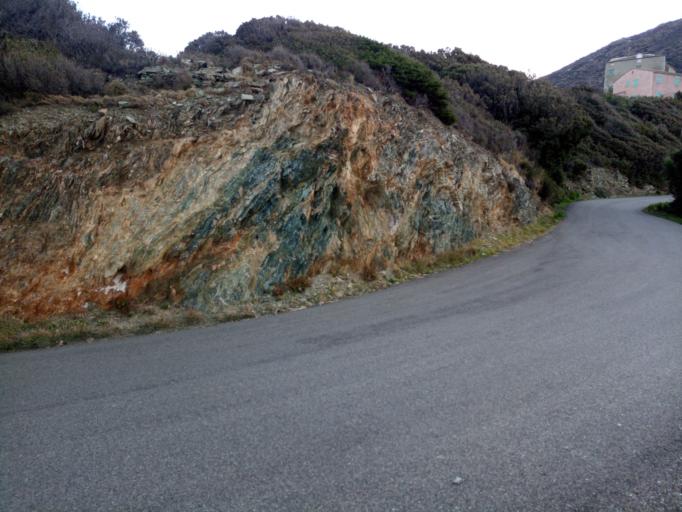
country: FR
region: Corsica
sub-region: Departement de la Haute-Corse
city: Brando
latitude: 42.9489
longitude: 9.3617
